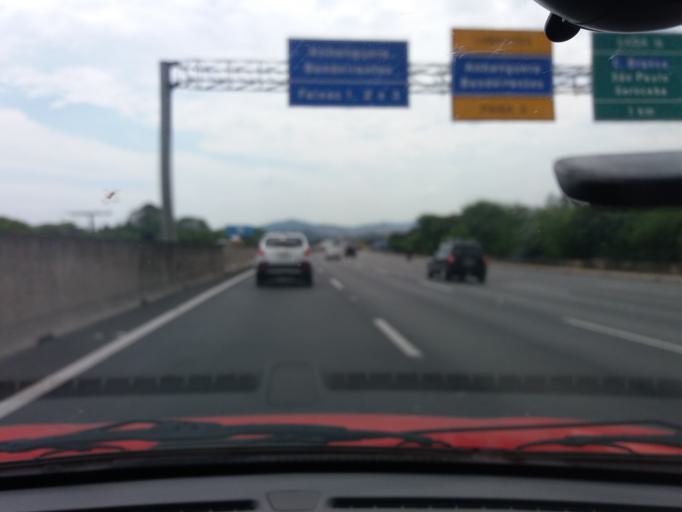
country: BR
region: Sao Paulo
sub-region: Carapicuiba
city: Carapicuiba
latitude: -23.5321
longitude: -46.8180
